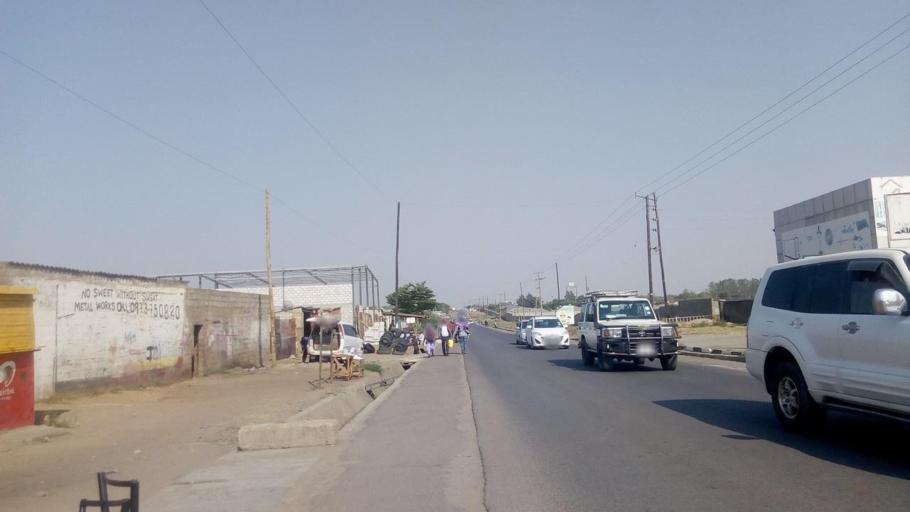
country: ZM
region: Lusaka
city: Lusaka
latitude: -15.3697
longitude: 28.2883
